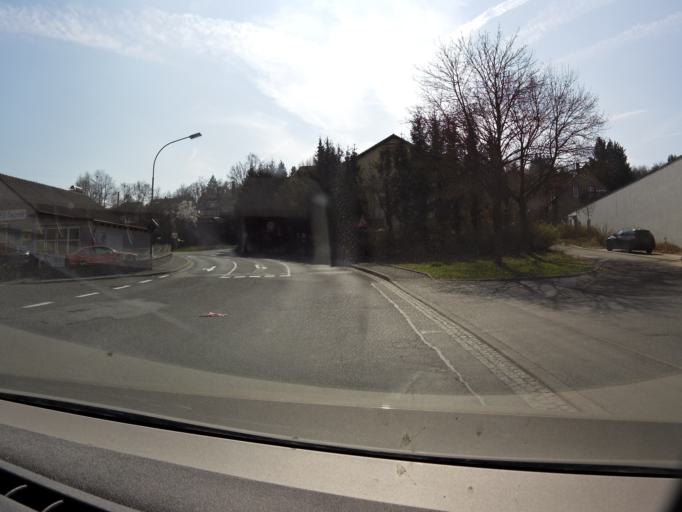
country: DE
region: Bavaria
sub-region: Regierungsbezirk Unterfranken
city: Ochsenfurt
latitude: 49.6620
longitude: 10.0682
